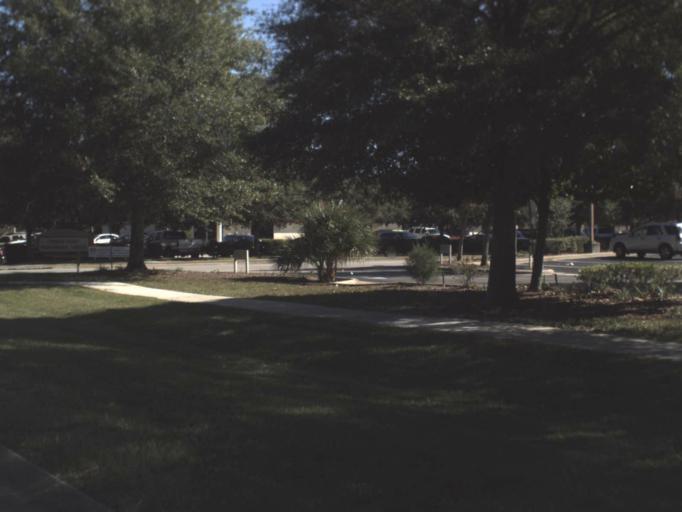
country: US
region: Florida
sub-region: Flagler County
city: Palm Coast
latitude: 29.5505
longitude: -81.2358
